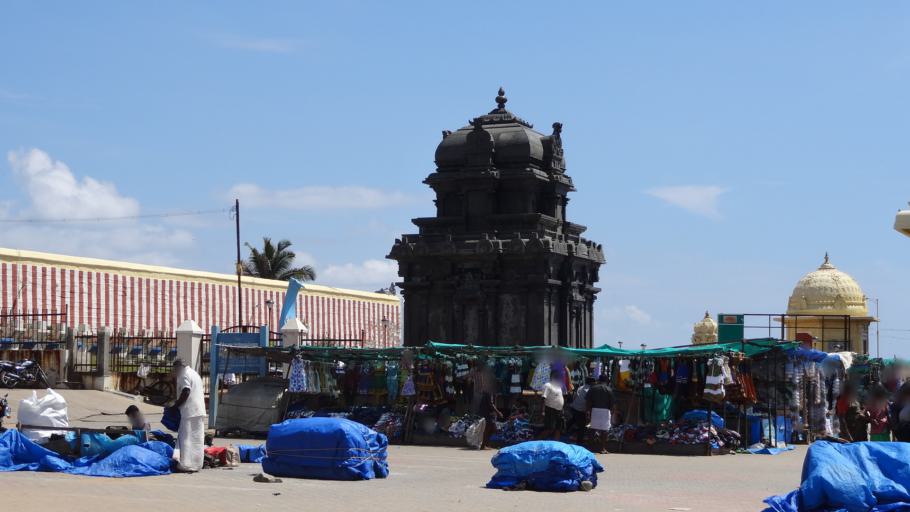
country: IN
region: Tamil Nadu
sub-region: Kanniyakumari
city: Kanniyakumari
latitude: 8.0785
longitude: 77.5503
